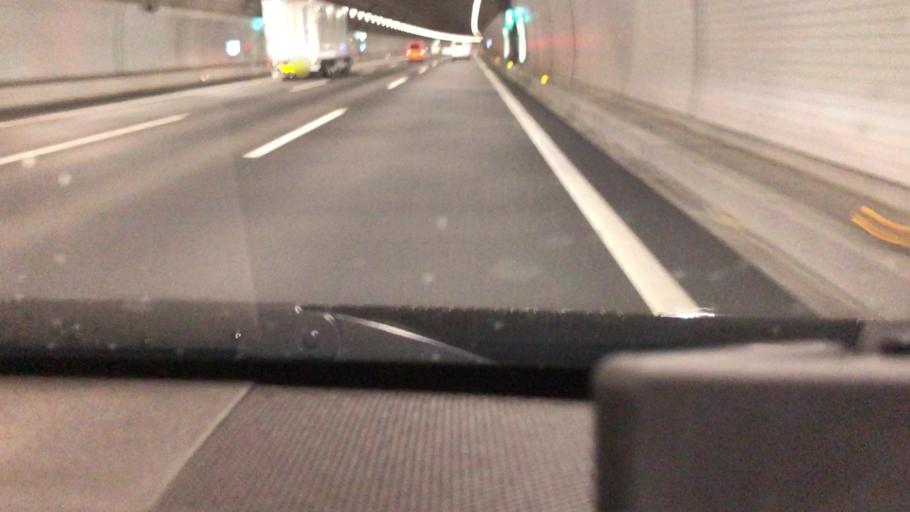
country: JP
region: Shizuoka
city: Kanaya
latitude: 34.8434
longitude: 138.0646
